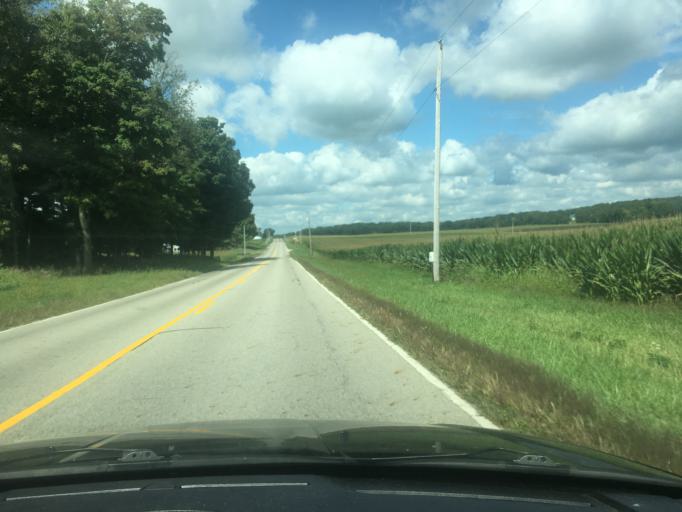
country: US
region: Ohio
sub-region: Logan County
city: West Liberty
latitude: 40.2366
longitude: -83.7104
